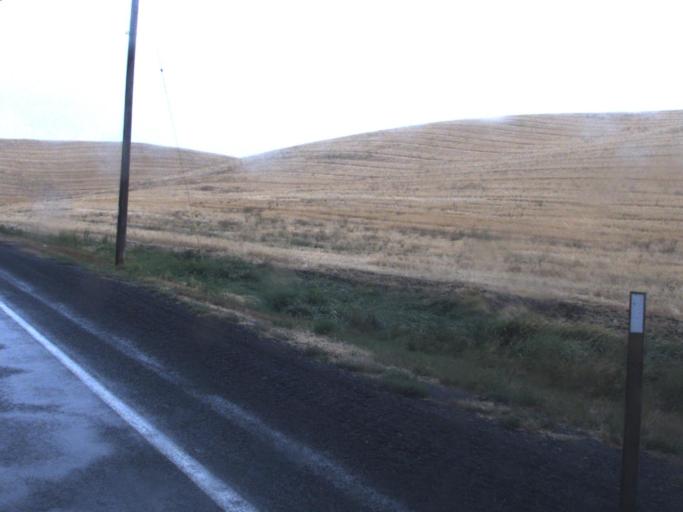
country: US
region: Washington
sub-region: Whitman County
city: Colfax
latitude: 47.0037
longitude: -117.4069
